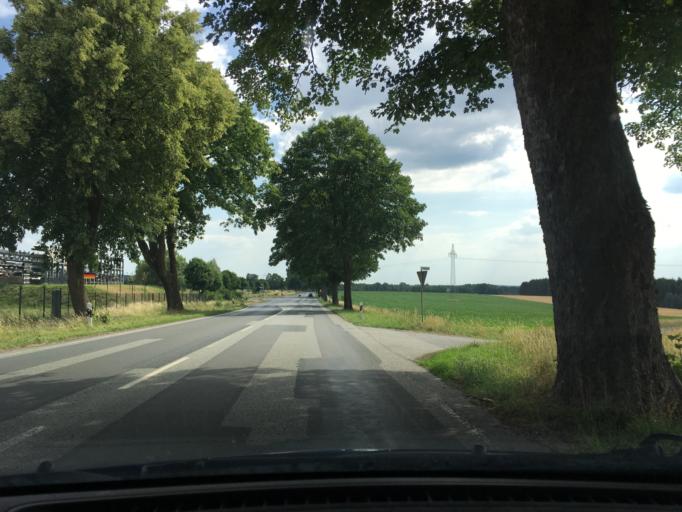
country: DE
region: Lower Saxony
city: Kakenstorf
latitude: 53.3234
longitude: 9.8104
